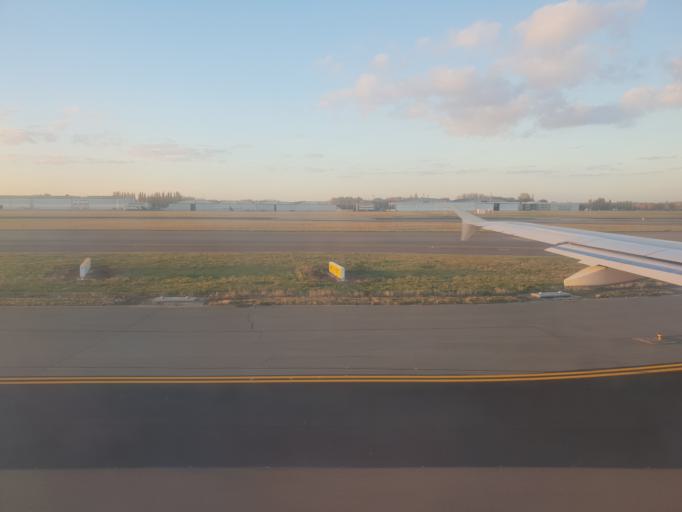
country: BE
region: Flanders
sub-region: Provincie Vlaams-Brabant
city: Steenokkerzeel
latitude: 50.9081
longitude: 4.4954
